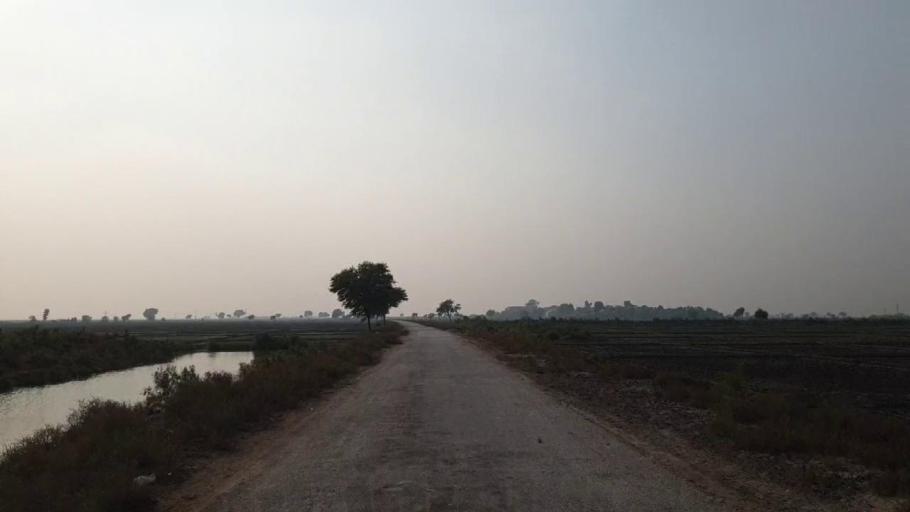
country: PK
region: Sindh
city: Bhan
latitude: 26.4883
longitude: 67.7112
